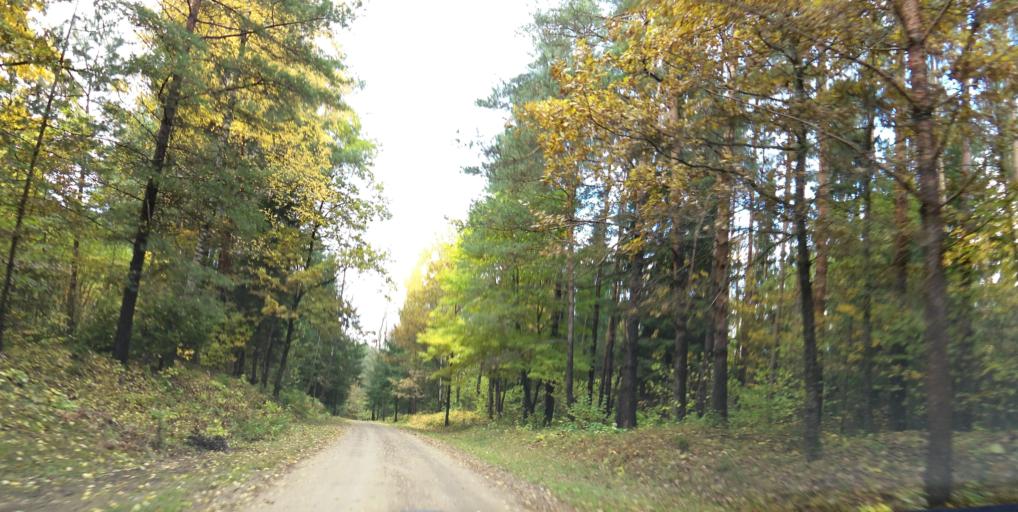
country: LT
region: Vilnius County
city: Vilkpede
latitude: 54.6491
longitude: 25.2542
